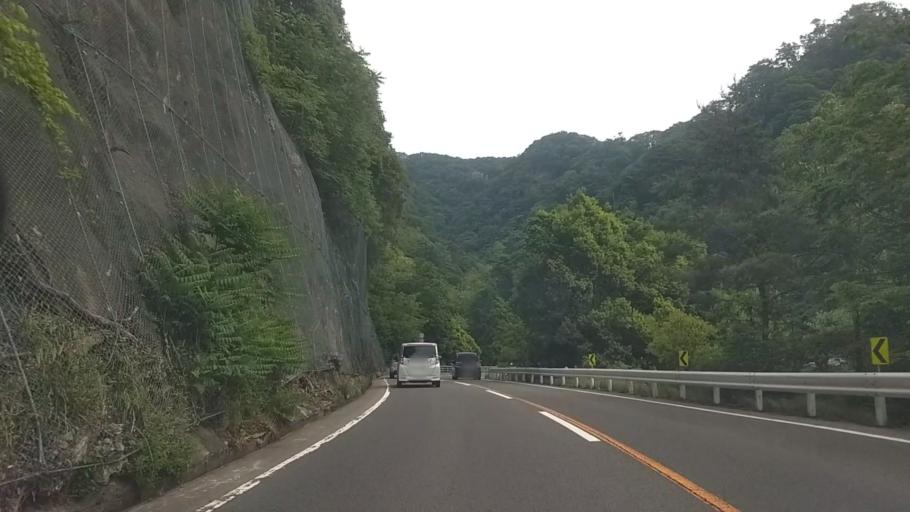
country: JP
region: Yamanashi
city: Isawa
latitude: 35.5626
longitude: 138.5934
